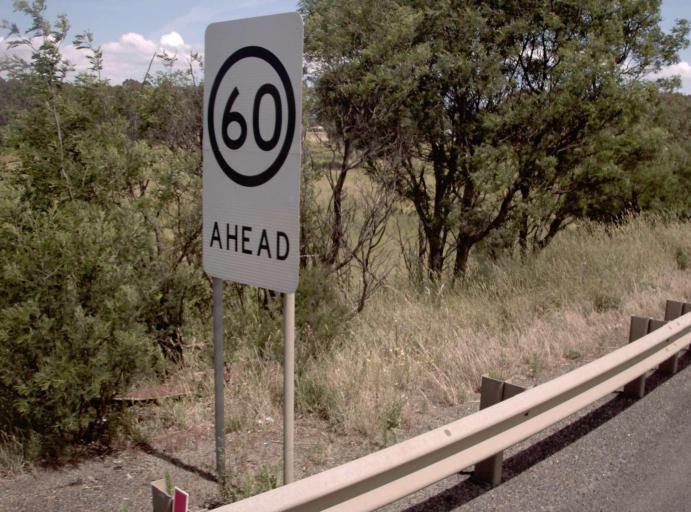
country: AU
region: Victoria
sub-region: Wellington
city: Heyfield
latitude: -38.1451
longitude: 146.7916
